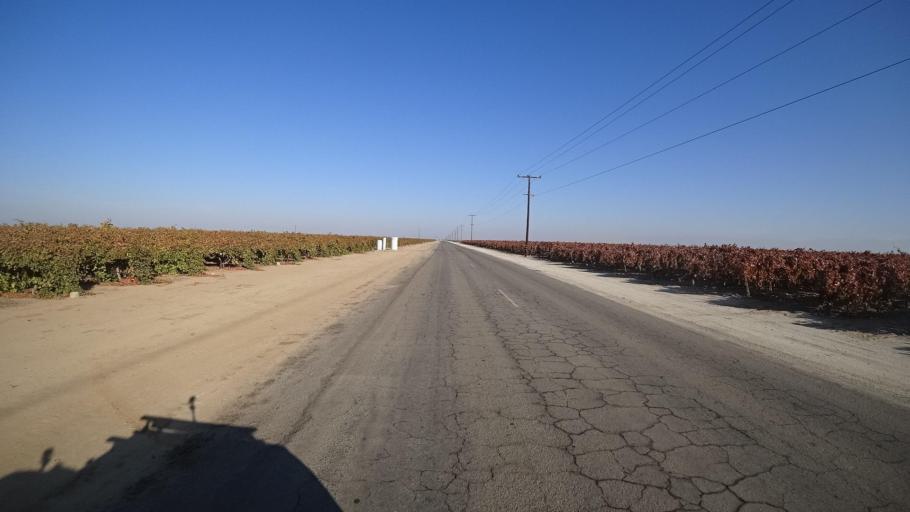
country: US
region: California
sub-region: Tulare County
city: Richgrove
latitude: 35.7483
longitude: -119.1696
